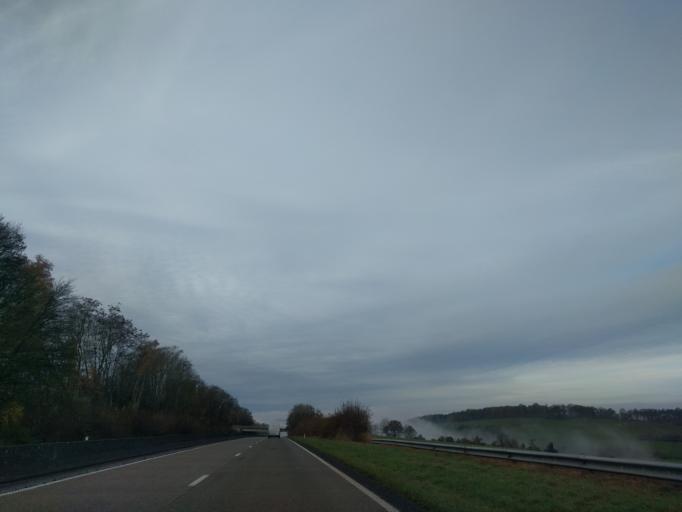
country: BE
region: Wallonia
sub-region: Province de Namur
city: Dinant
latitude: 50.2388
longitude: 4.9495
